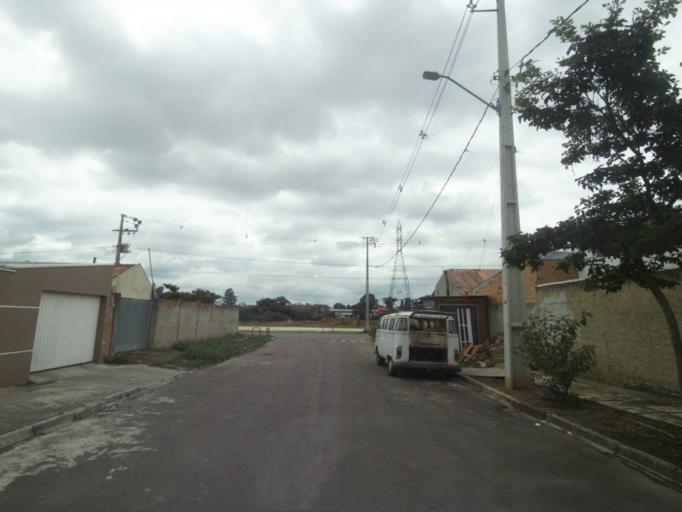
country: BR
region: Parana
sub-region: Pinhais
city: Pinhais
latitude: -25.4469
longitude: -49.1998
